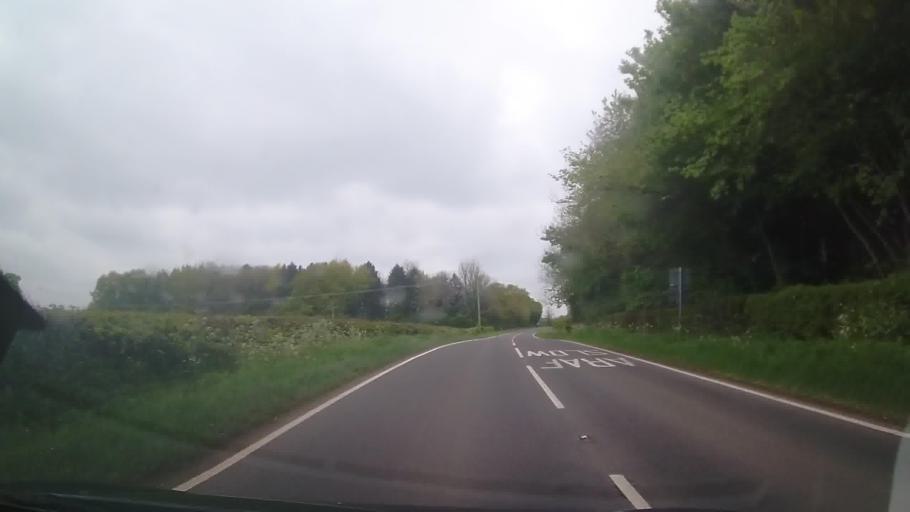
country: GB
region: Wales
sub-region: Wrexham
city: Ruabon
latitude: 52.9813
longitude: -3.0117
